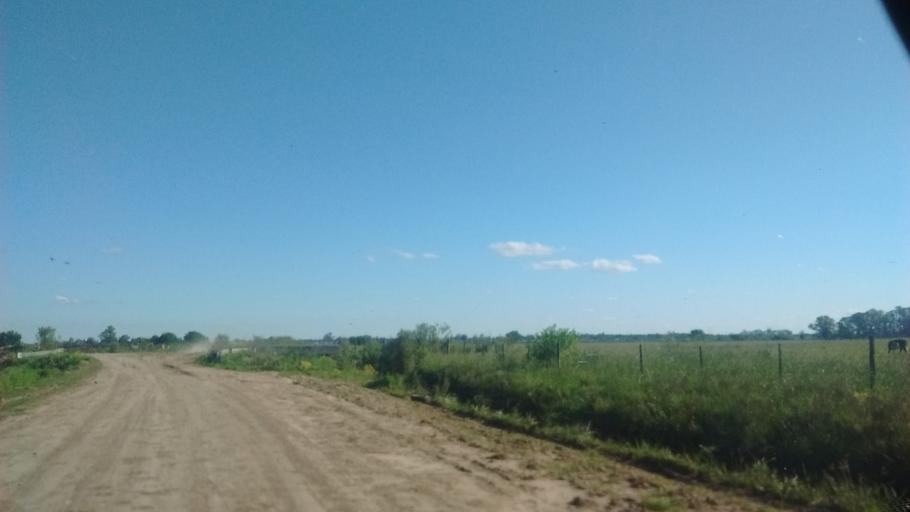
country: AR
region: Santa Fe
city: Funes
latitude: -32.8856
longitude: -60.7981
